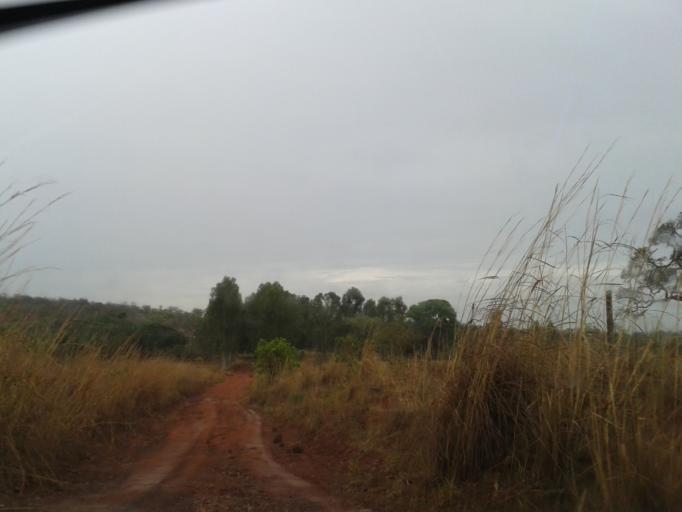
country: BR
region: Minas Gerais
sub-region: Campina Verde
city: Campina Verde
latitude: -19.3156
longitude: -49.5092
